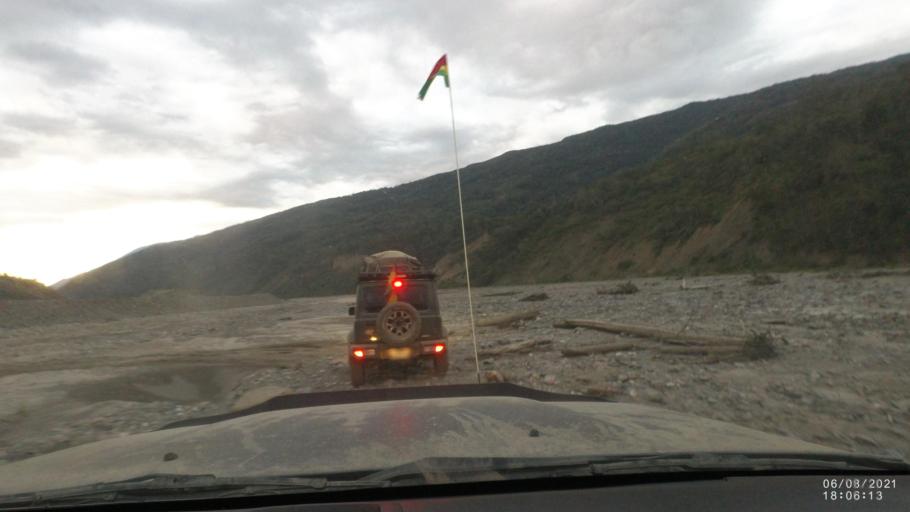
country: BO
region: La Paz
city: Quime
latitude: -16.4711
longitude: -66.7861
